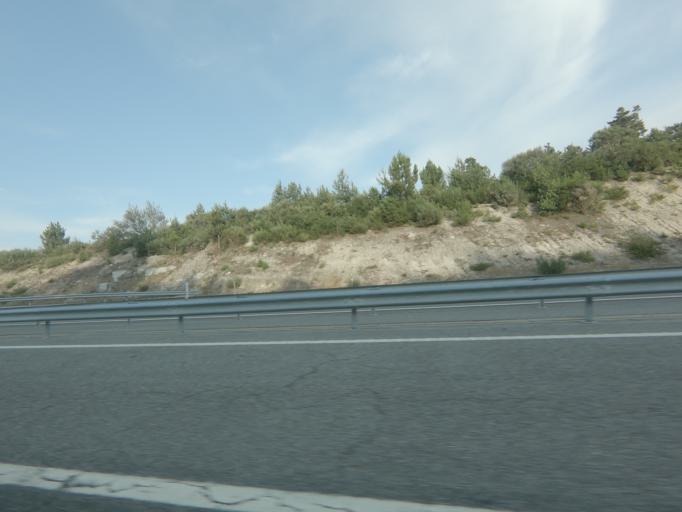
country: PT
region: Vila Real
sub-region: Vila Pouca de Aguiar
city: Vila Pouca de Aguiar
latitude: 41.4942
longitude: -7.6582
